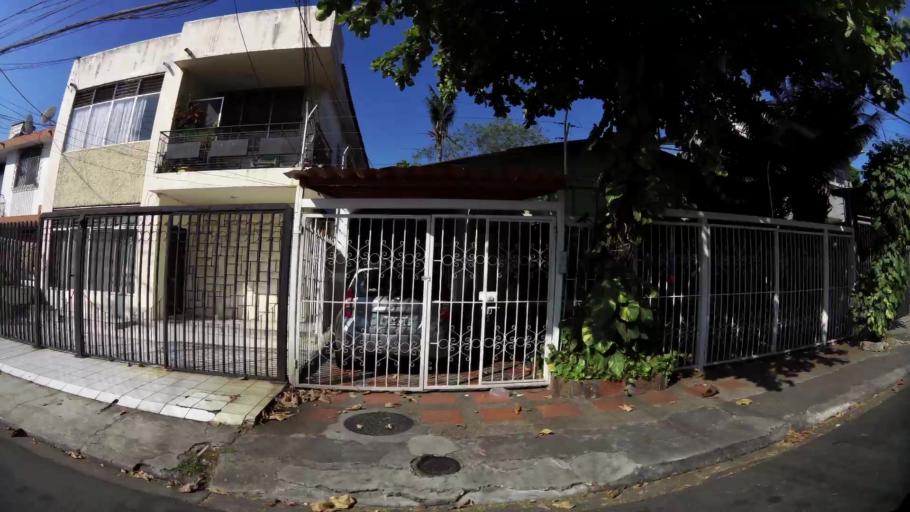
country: EC
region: Guayas
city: Guayaquil
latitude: -2.1756
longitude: -79.9012
